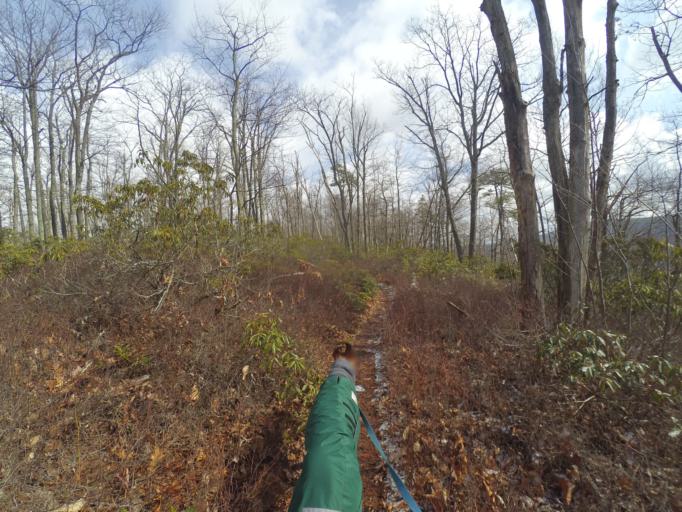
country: US
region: Pennsylvania
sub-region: Centre County
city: Boalsburg
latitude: 40.7469
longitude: -77.7389
